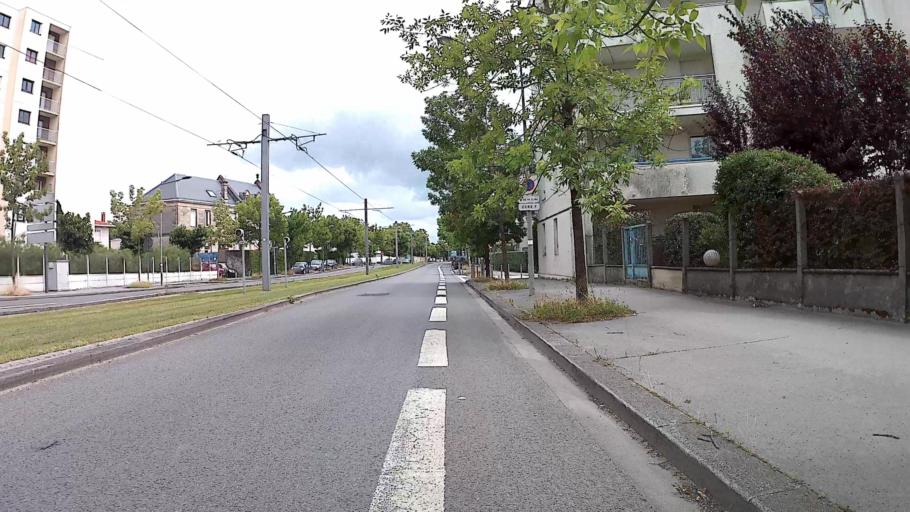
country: FR
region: Aquitaine
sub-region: Departement de la Gironde
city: Merignac
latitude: 44.8275
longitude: -0.6134
